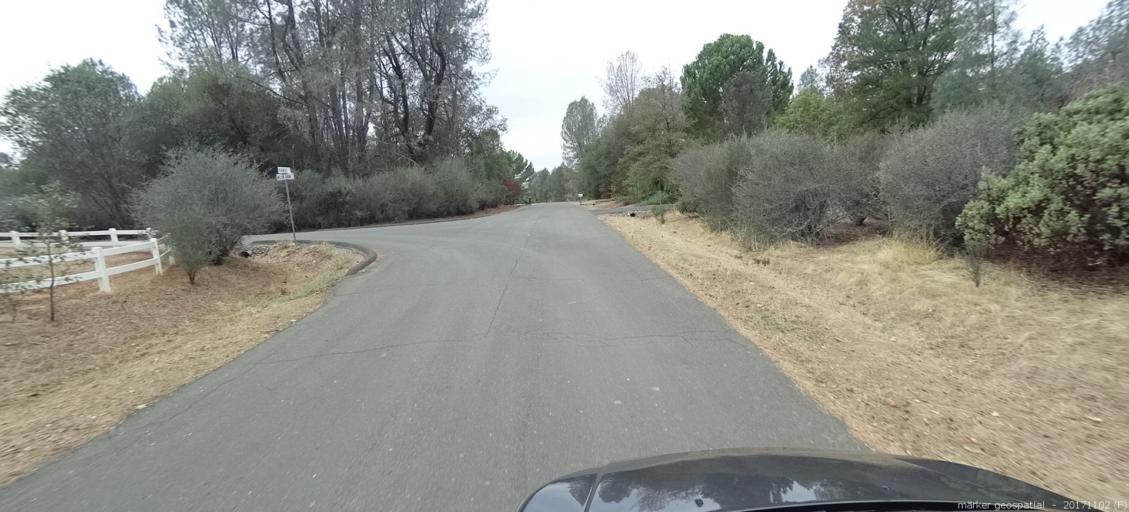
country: US
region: California
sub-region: Shasta County
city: Shasta Lake
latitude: 40.6607
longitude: -122.3201
